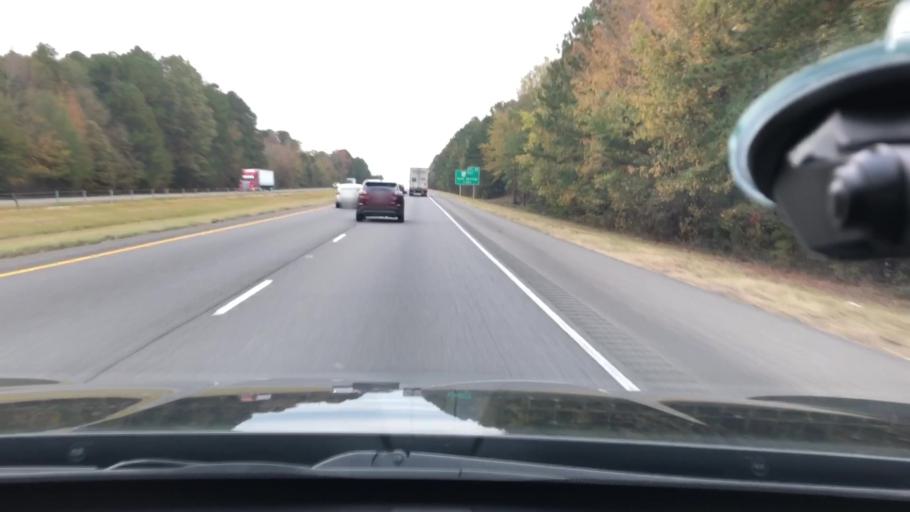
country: US
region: Arkansas
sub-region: Clark County
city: Arkadelphia
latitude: 34.0548
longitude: -93.1315
